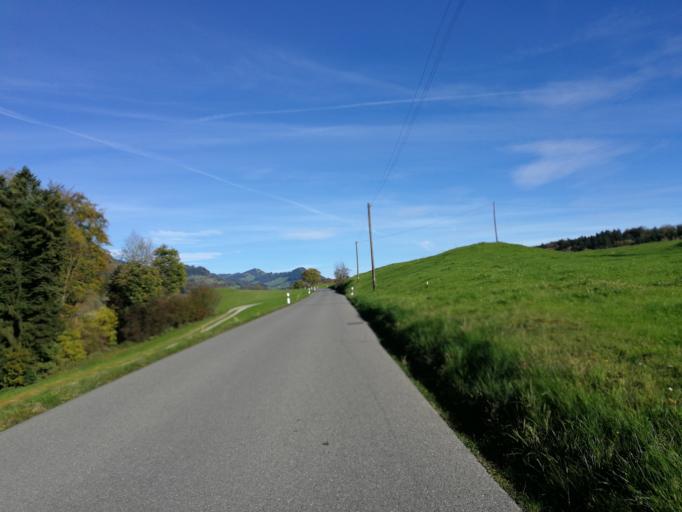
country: CH
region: Saint Gallen
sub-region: Wahlkreis See-Gaster
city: Eschenbach
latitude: 47.2490
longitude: 8.9021
